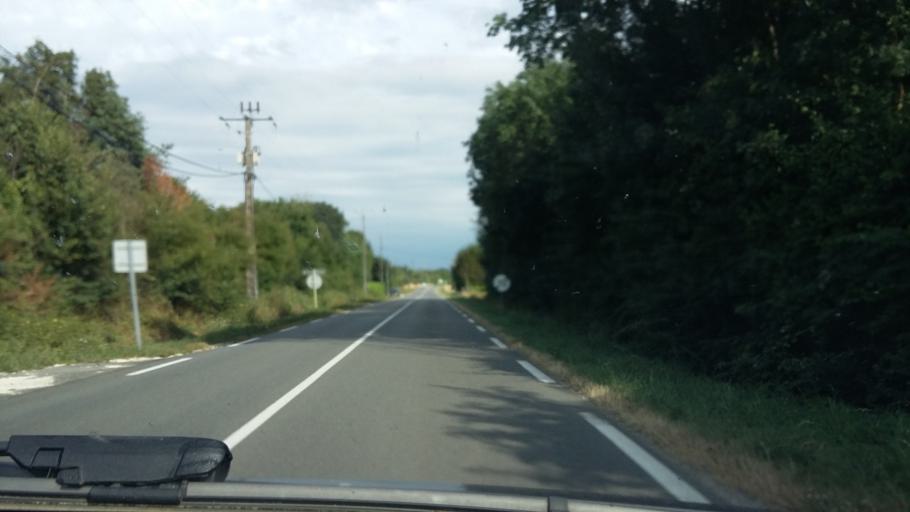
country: FR
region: Poitou-Charentes
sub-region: Departement de la Charente
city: Balzac
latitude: 45.7068
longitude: 0.0851
